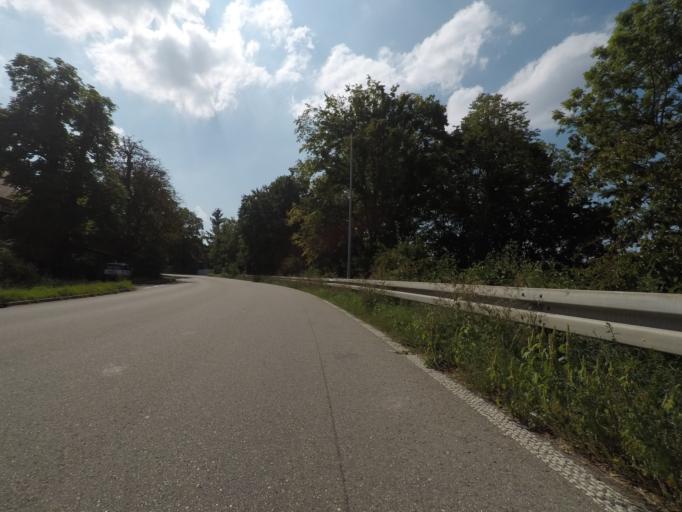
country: DE
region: Baden-Wuerttemberg
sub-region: Regierungsbezirk Stuttgart
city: Winterbach
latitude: 48.7912
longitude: 9.4665
